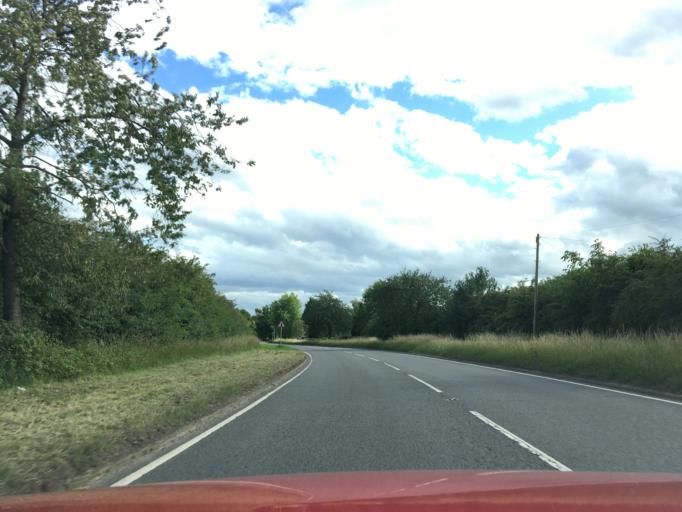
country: GB
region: England
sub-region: Warwickshire
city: Hartshill
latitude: 52.5681
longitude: -1.4828
